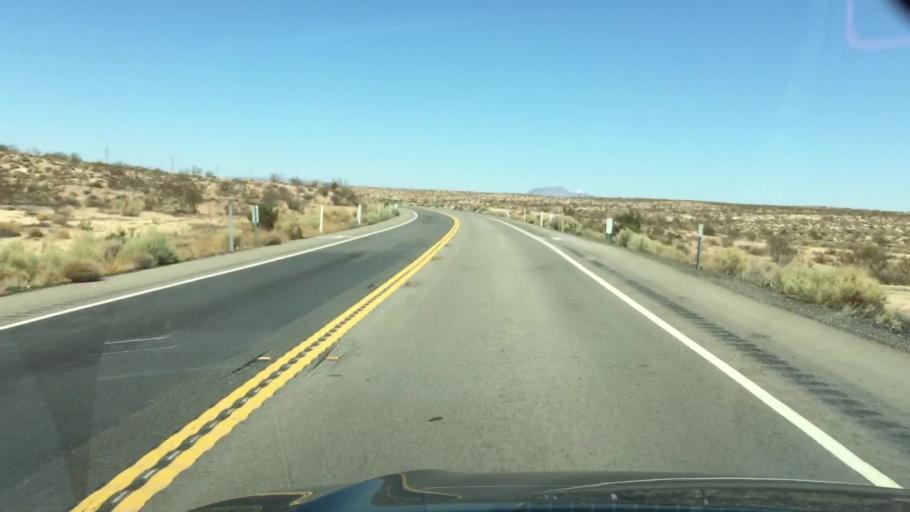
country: US
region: California
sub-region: Kern County
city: Boron
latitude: 35.0709
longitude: -117.5592
